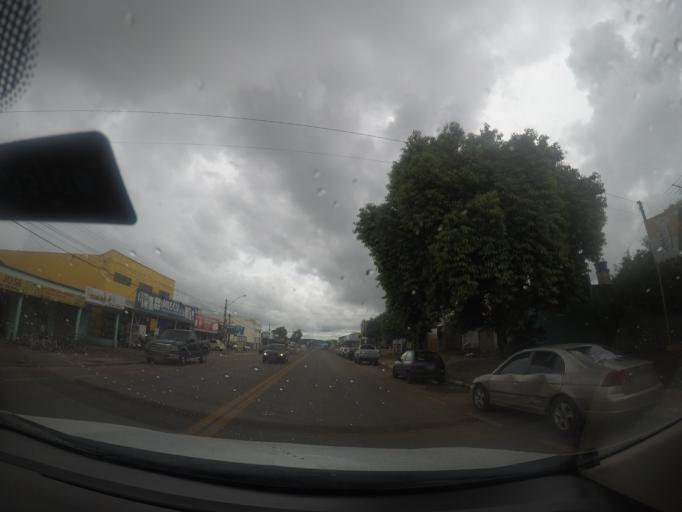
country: BR
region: Goias
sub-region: Trindade
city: Trindade
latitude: -16.6357
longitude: -49.3903
